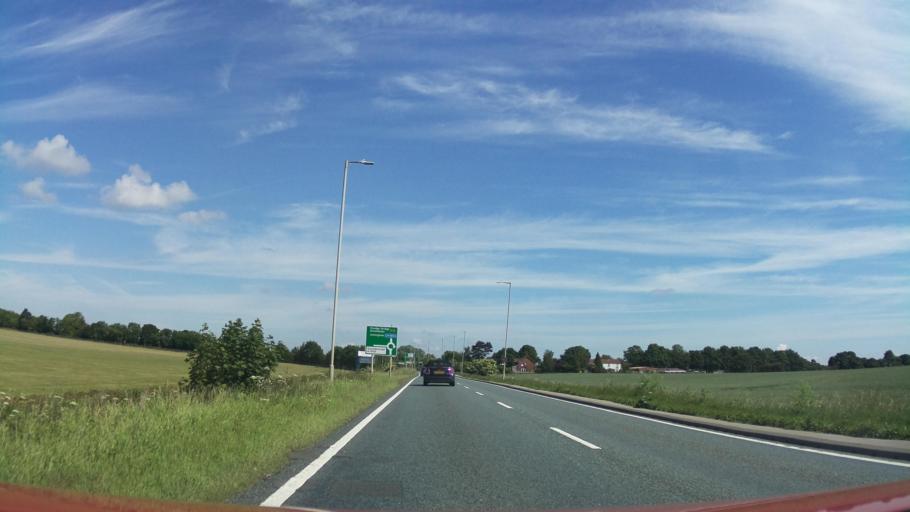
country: GB
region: England
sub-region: Lincolnshire
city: Burton
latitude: 53.2880
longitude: -0.5407
